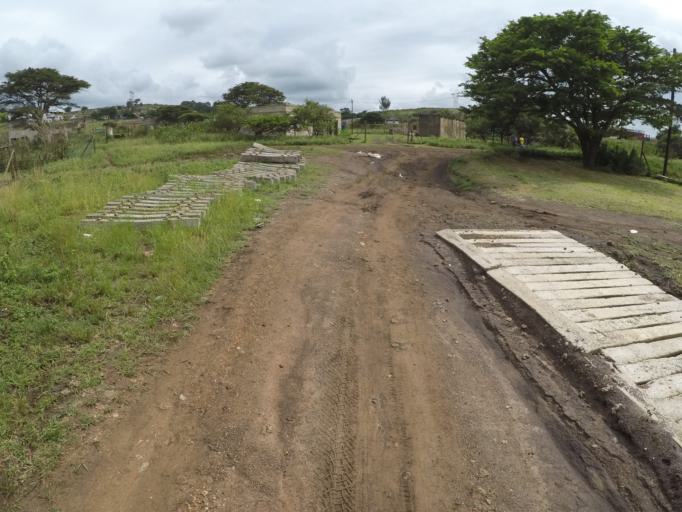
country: ZA
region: KwaZulu-Natal
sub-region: uThungulu District Municipality
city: Empangeni
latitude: -28.7121
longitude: 31.8537
